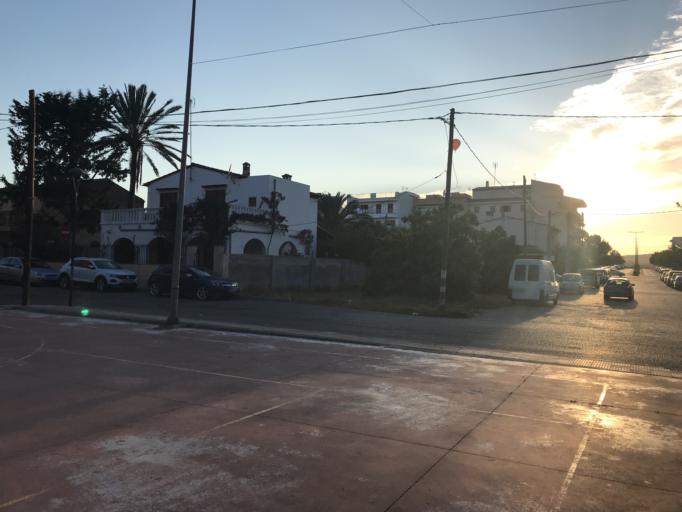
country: ES
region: Balearic Islands
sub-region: Illes Balears
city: Son Servera
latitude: 39.5624
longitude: 3.3716
